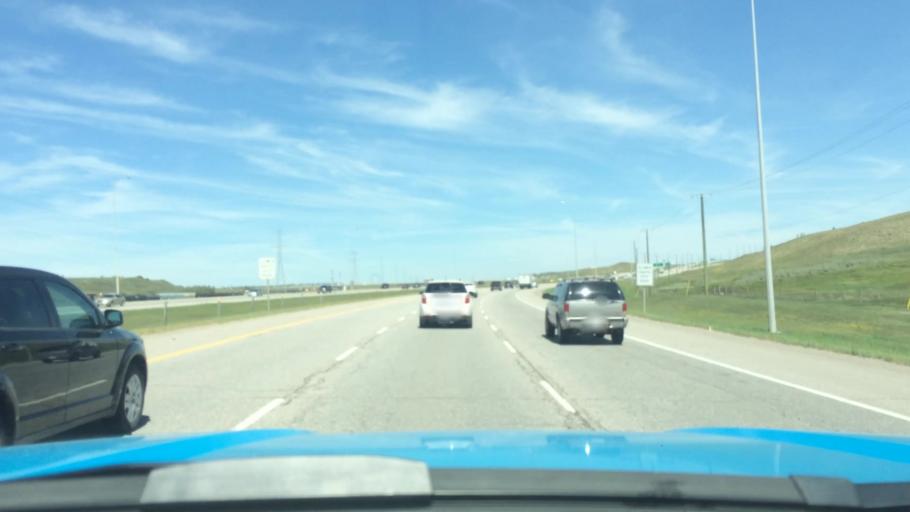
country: CA
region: Alberta
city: Calgary
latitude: 51.1299
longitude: -114.0454
